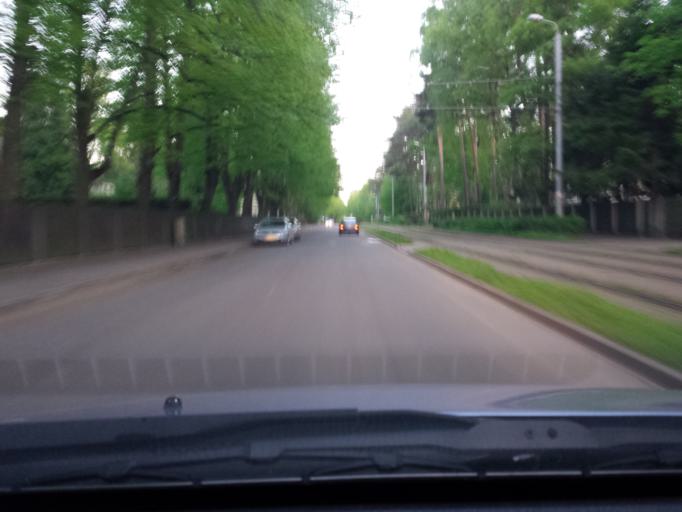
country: LV
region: Riga
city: Jaunciems
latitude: 56.9997
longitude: 24.1602
